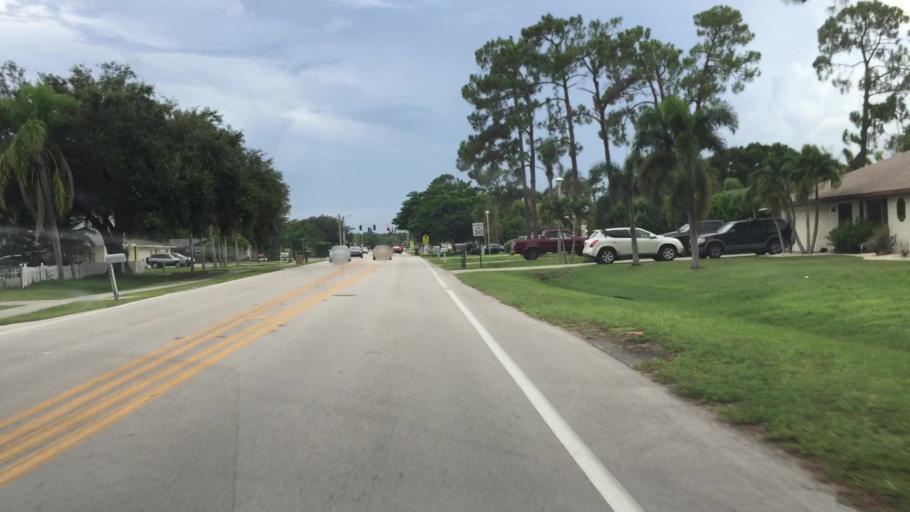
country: US
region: Florida
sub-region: Lee County
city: Villas
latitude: 26.5646
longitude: -81.8658
